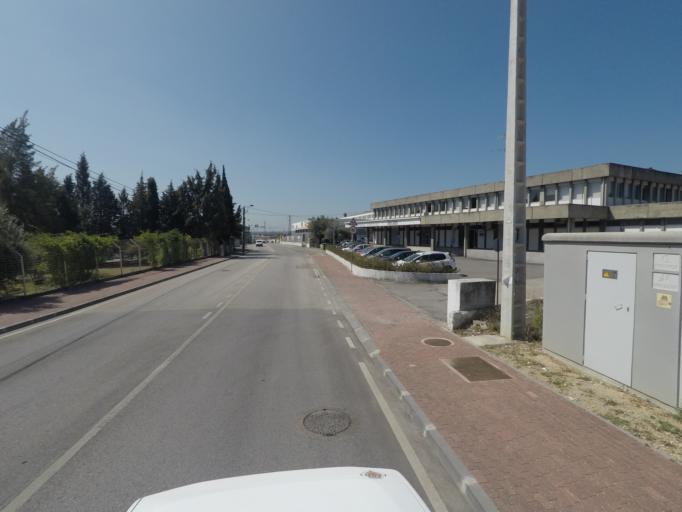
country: PT
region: Coimbra
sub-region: Coimbra
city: Coimbra
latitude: 40.2423
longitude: -8.4339
